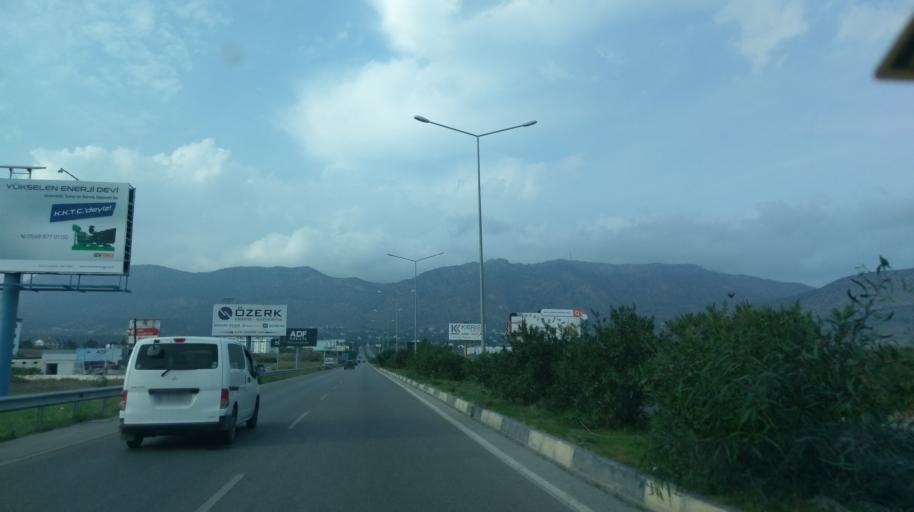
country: CY
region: Keryneia
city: Kyrenia
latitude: 35.2732
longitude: 33.2880
